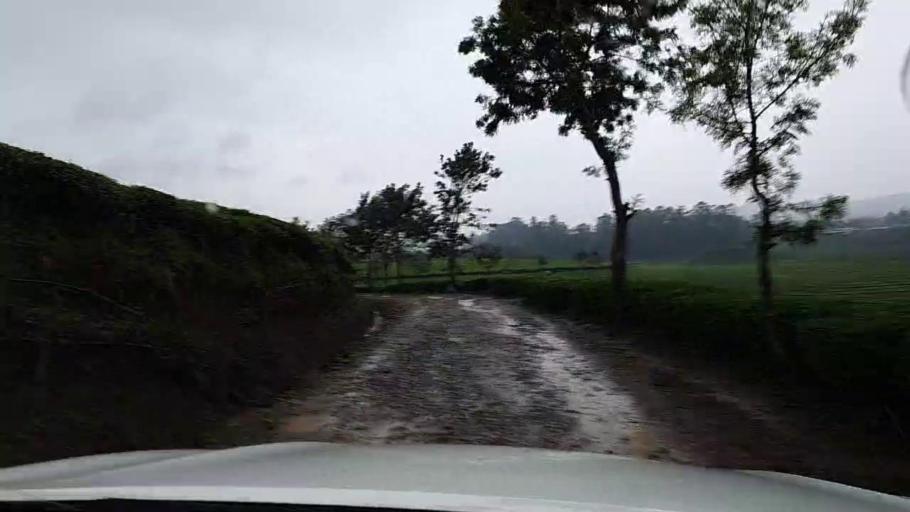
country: RW
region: Western Province
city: Cyangugu
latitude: -2.4565
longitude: 29.0403
